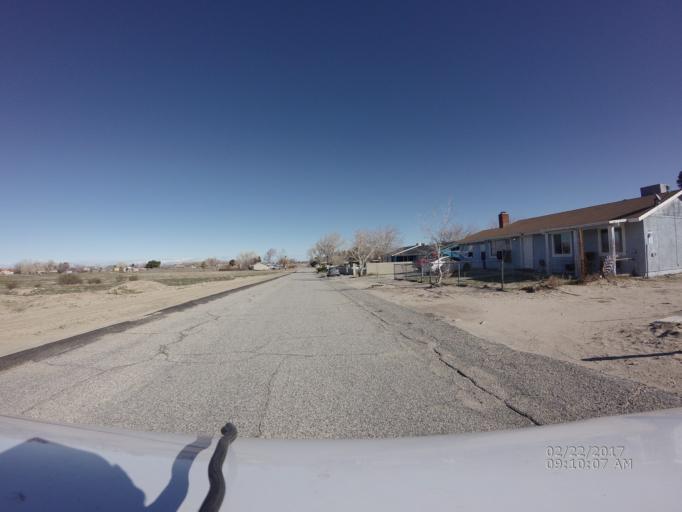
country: US
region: California
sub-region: Los Angeles County
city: Lake Los Angeles
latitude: 34.6188
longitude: -117.8580
